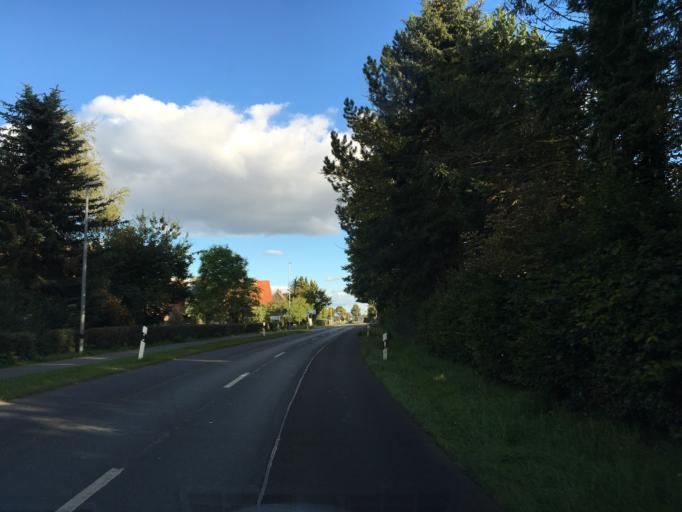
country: DE
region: Lower Saxony
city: Reppenstedt
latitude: 53.2475
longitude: 10.3662
